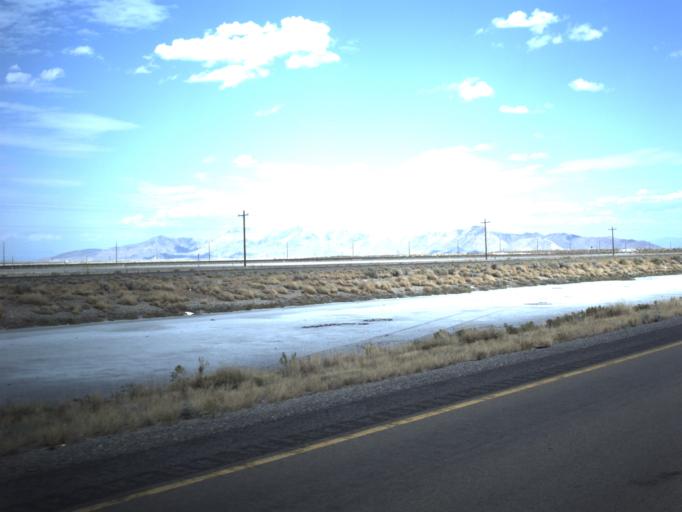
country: US
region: Utah
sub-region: Tooele County
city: Grantsville
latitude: 40.7508
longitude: -112.7042
